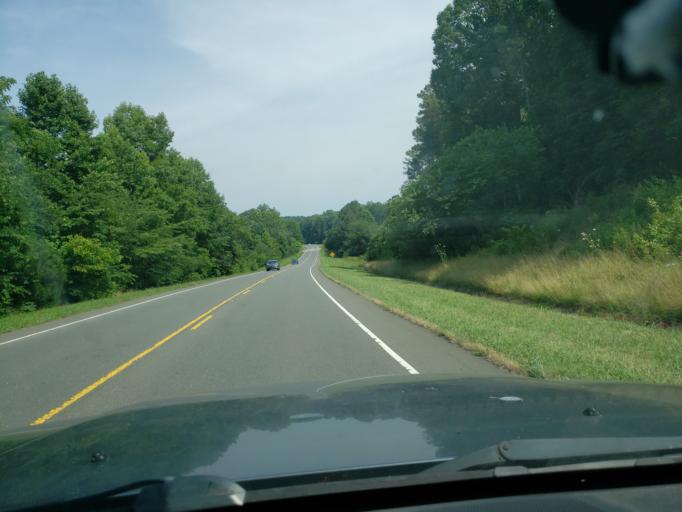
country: US
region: North Carolina
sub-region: Alamance County
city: Saxapahaw
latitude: 35.9454
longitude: -79.2480
